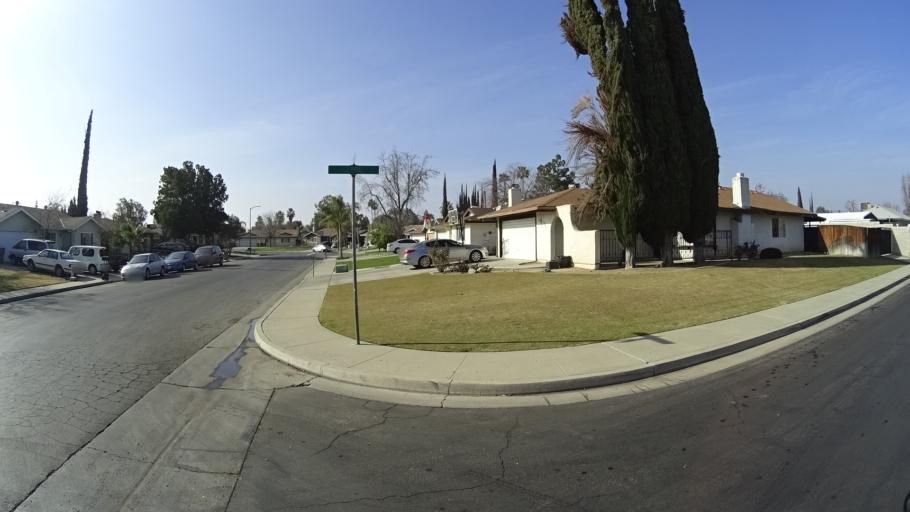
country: US
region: California
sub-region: Kern County
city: Bakersfield
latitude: 35.3276
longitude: -119.0626
